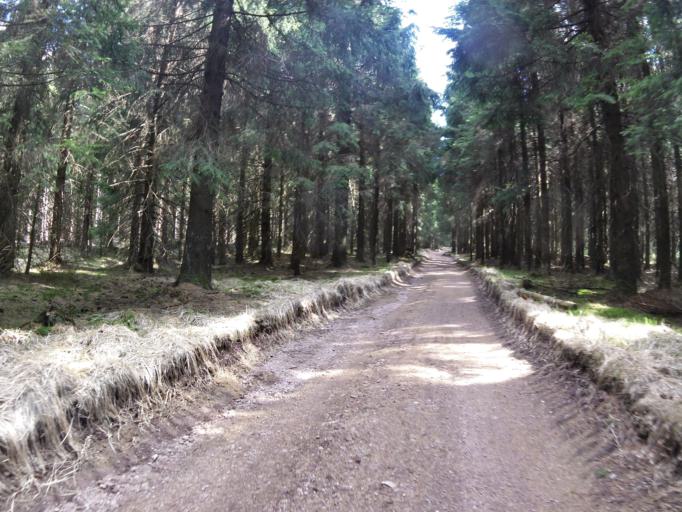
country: DE
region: Thuringia
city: Unterschonau
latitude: 50.7495
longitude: 10.5706
